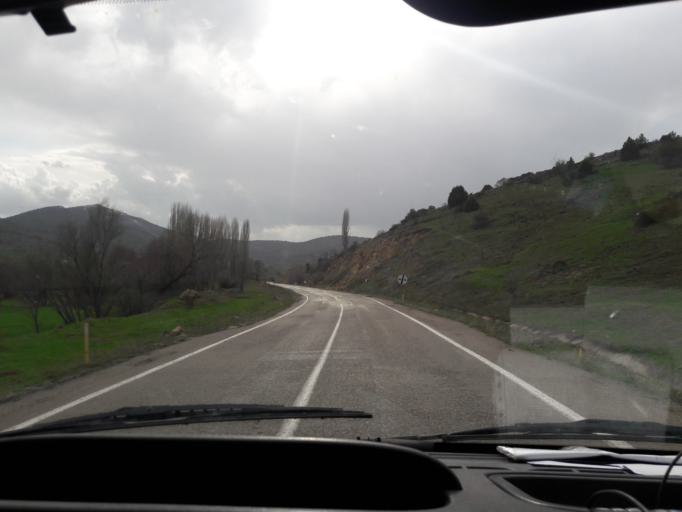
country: TR
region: Giresun
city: Alucra
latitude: 40.2651
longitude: 38.9061
